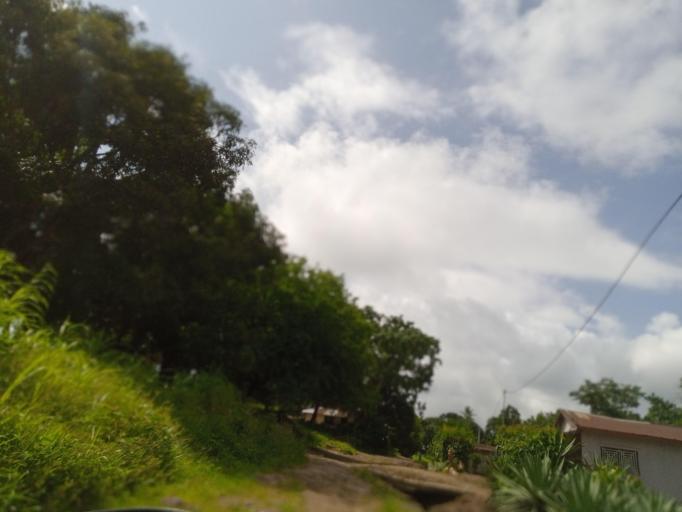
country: SL
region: Northern Province
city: Masoyila
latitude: 8.6046
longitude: -13.2051
